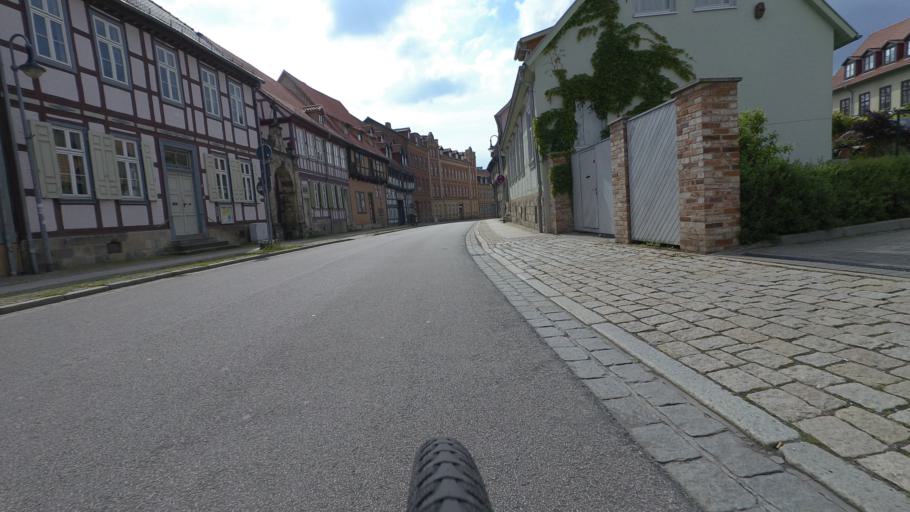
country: DE
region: Saxony-Anhalt
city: Halberstadt
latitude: 51.8946
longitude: 11.0448
